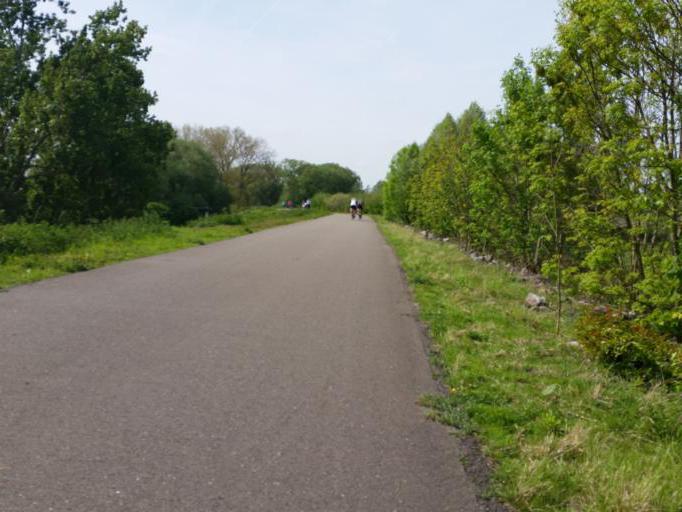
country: BE
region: Flanders
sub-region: Provincie Antwerpen
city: Boom
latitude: 51.0774
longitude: 4.3894
